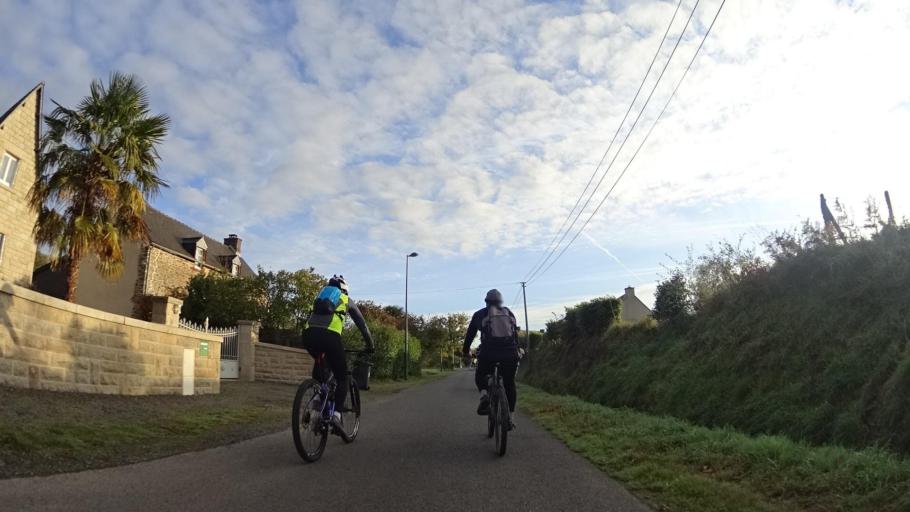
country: FR
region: Brittany
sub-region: Departement des Cotes-d'Armor
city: Evran
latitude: 48.3813
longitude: -1.9692
